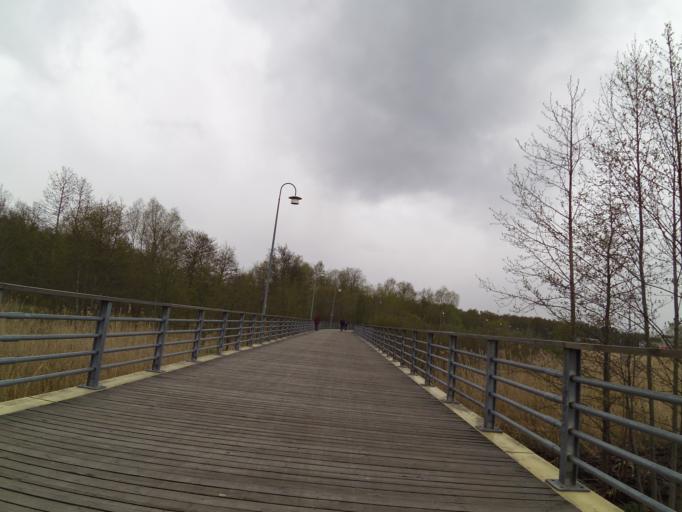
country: EE
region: Harju
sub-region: Tallinna linn
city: Tallinn
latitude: 59.4303
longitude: 24.6726
